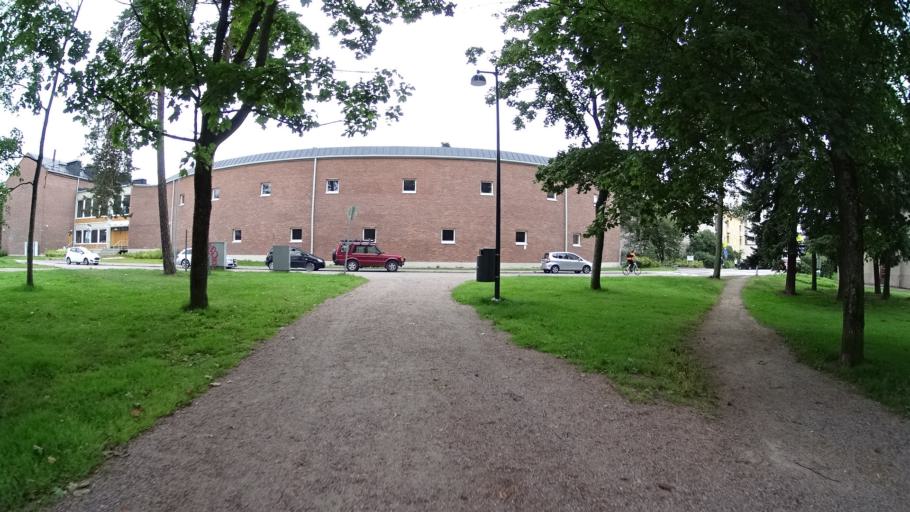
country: FI
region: Uusimaa
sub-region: Helsinki
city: Helsinki
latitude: 60.1925
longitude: 24.9020
